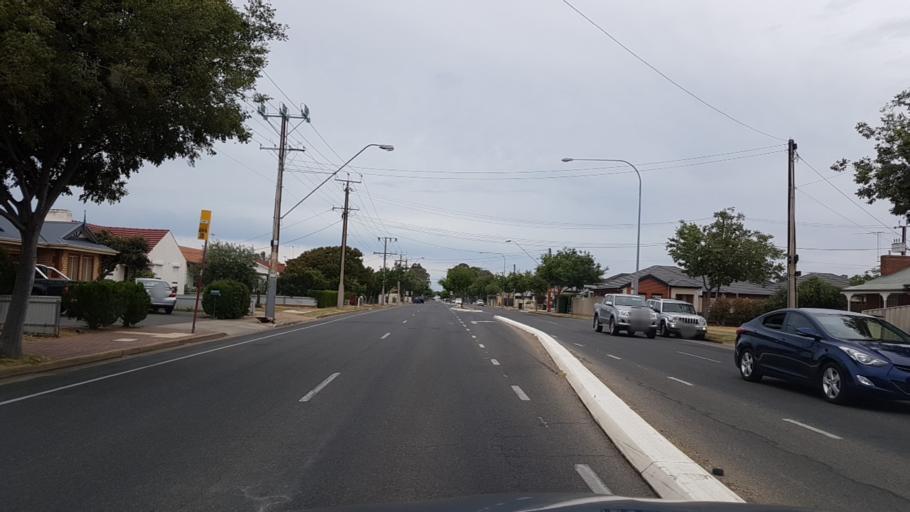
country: AU
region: South Australia
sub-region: Charles Sturt
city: Findon
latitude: -34.9010
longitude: 138.5406
